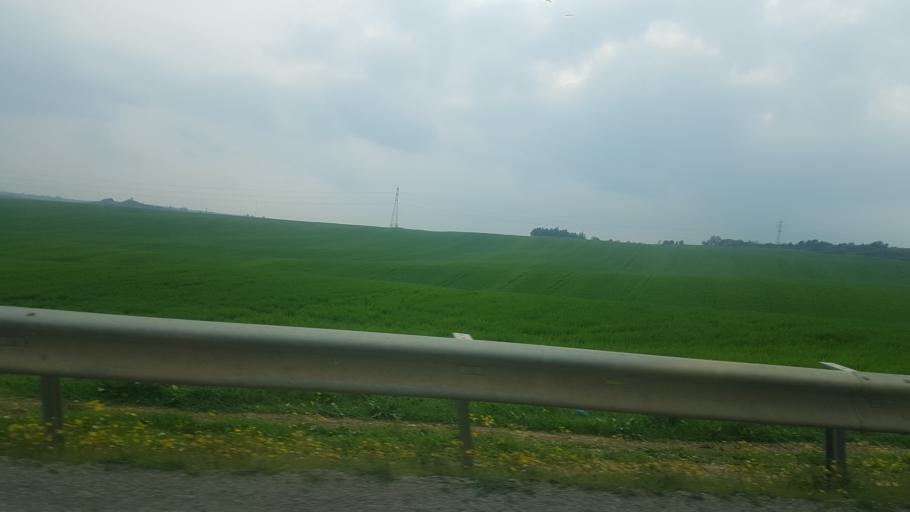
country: TR
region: Mersin
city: Yenice
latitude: 37.0730
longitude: 35.1693
